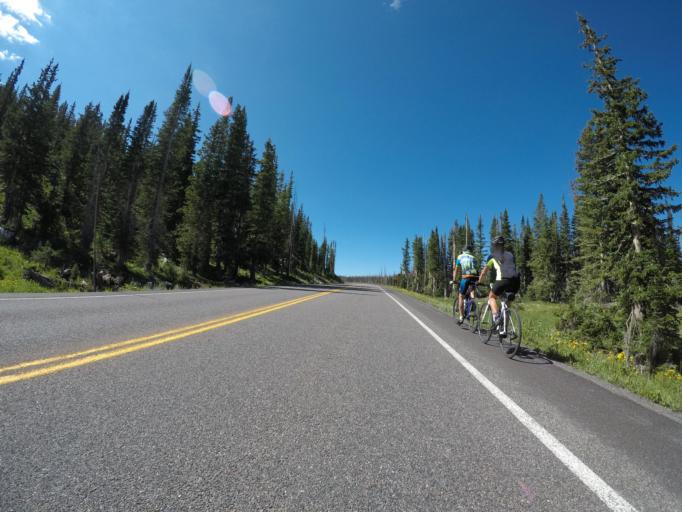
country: US
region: Wyoming
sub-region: Carbon County
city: Saratoga
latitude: 41.3161
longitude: -106.3587
